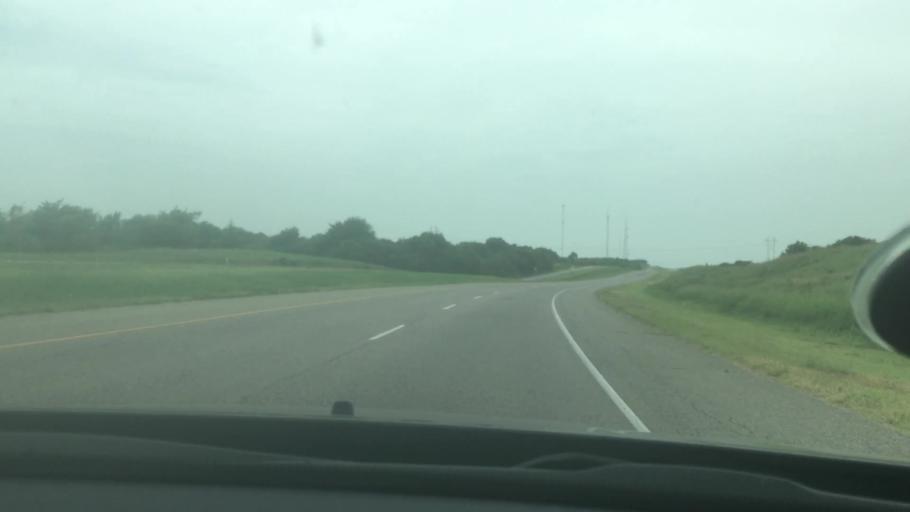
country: US
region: Oklahoma
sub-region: Pontotoc County
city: Ada
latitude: 34.6909
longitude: -96.7445
